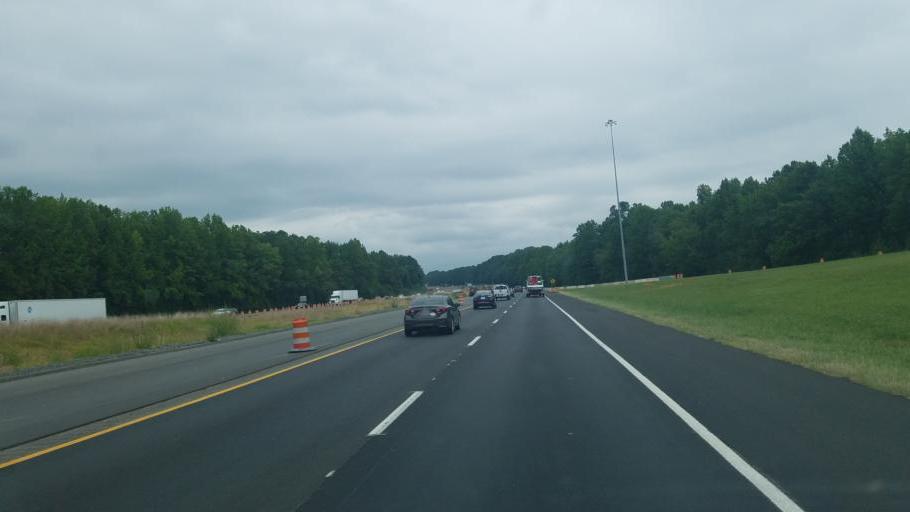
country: US
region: North Carolina
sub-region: Mecklenburg County
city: Huntersville
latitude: 35.4101
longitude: -80.8575
